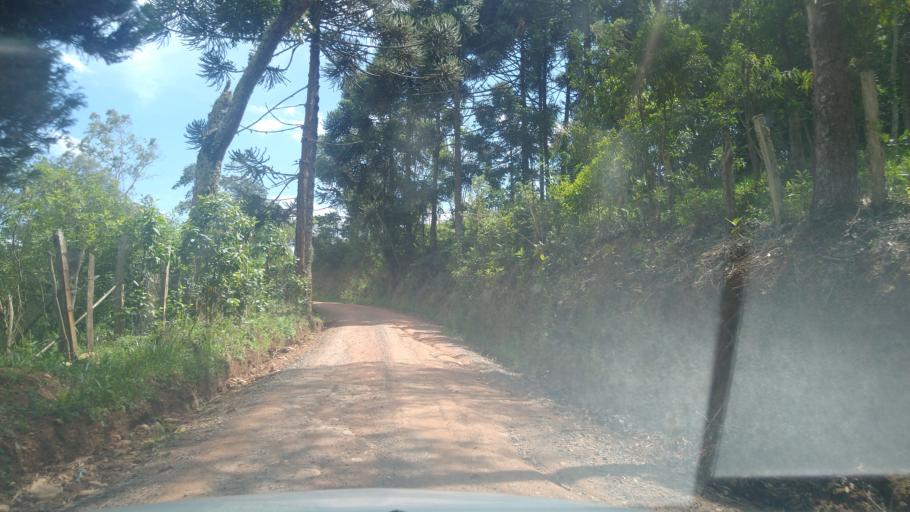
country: BR
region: Minas Gerais
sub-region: Extrema
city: Extrema
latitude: -22.7394
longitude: -46.2954
